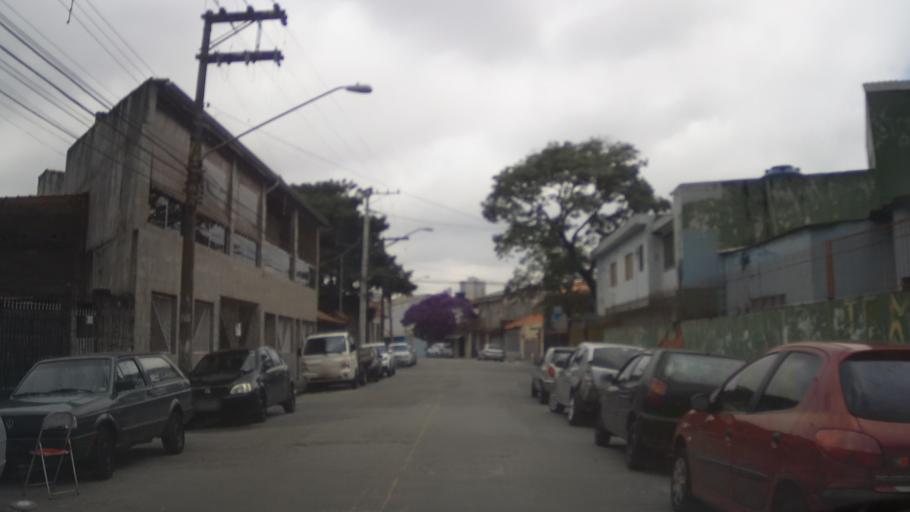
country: BR
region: Sao Paulo
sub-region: Guarulhos
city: Guarulhos
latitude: -23.4720
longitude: -46.5531
